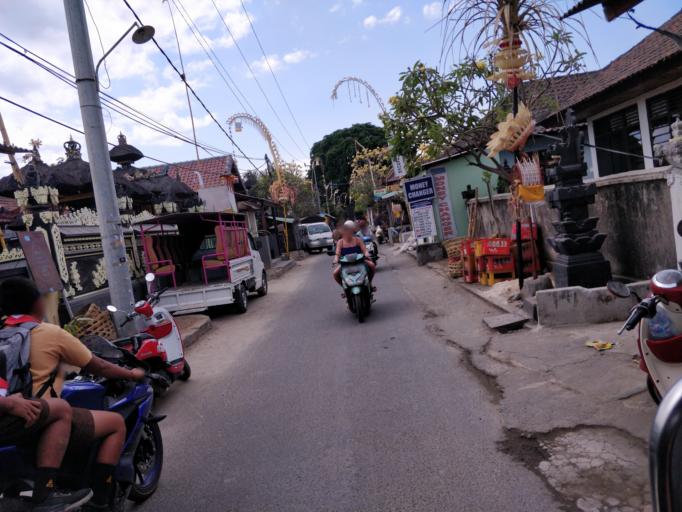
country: ID
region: Bali
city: Jungutbatu Kaja Dua
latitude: -8.6751
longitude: 115.4480
